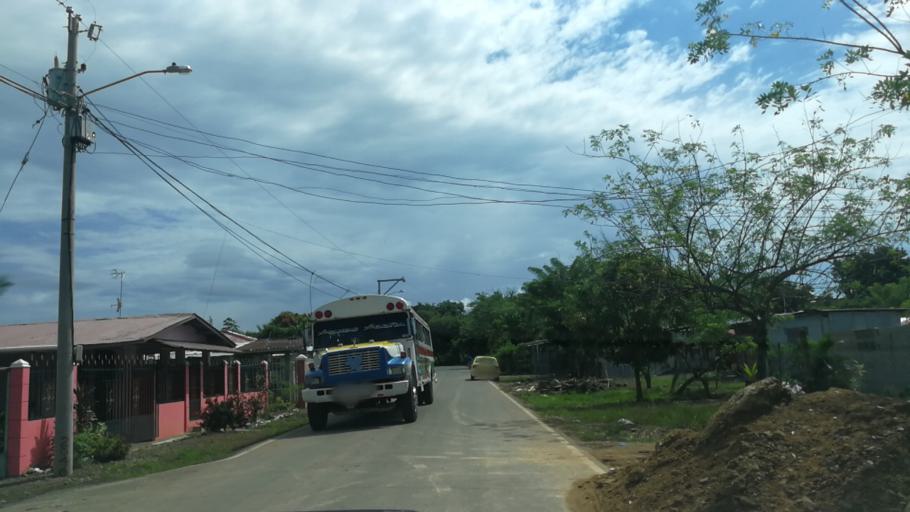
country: PA
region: Panama
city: Paso Blanco
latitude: 9.1360
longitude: -79.2528
